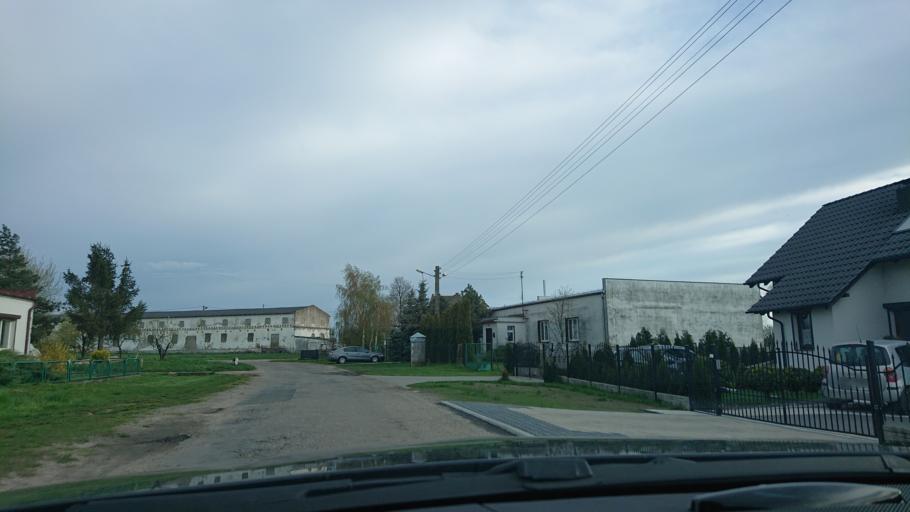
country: PL
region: Greater Poland Voivodeship
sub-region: Powiat gnieznienski
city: Lubowo
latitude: 52.5726
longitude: 17.4736
